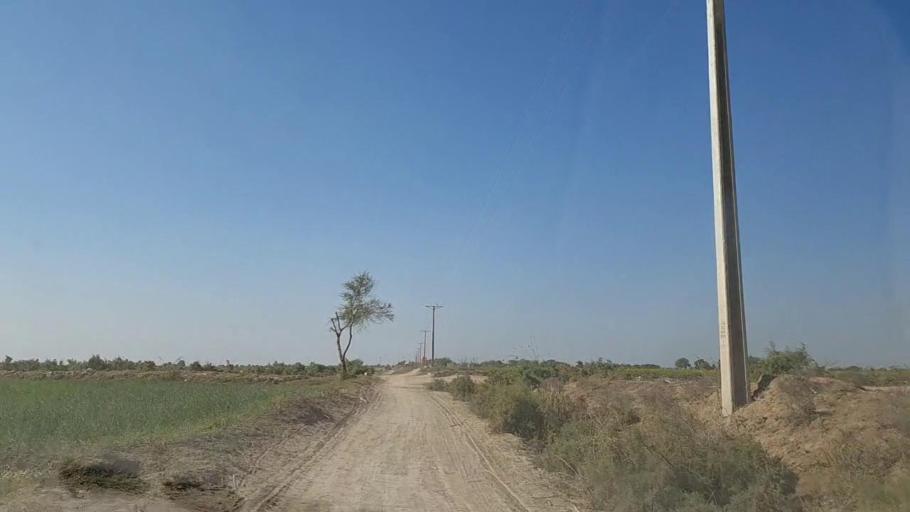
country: PK
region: Sindh
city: Digri
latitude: 25.1275
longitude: 69.0635
